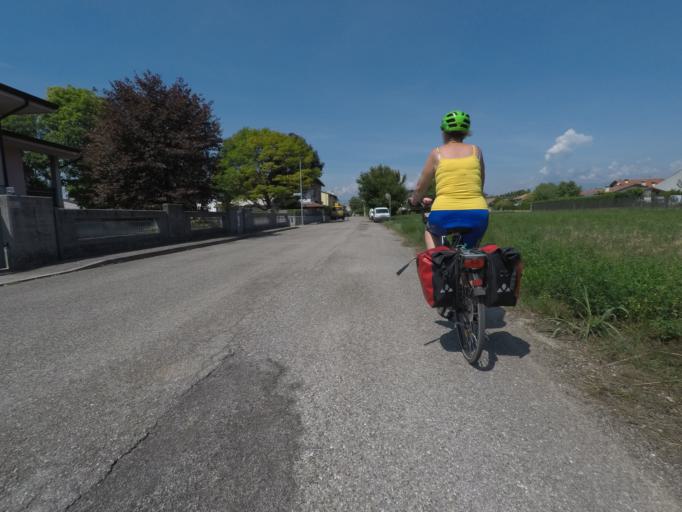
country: IT
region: Friuli Venezia Giulia
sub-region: Provincia di Udine
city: Dignano
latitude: 46.0844
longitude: 12.9449
